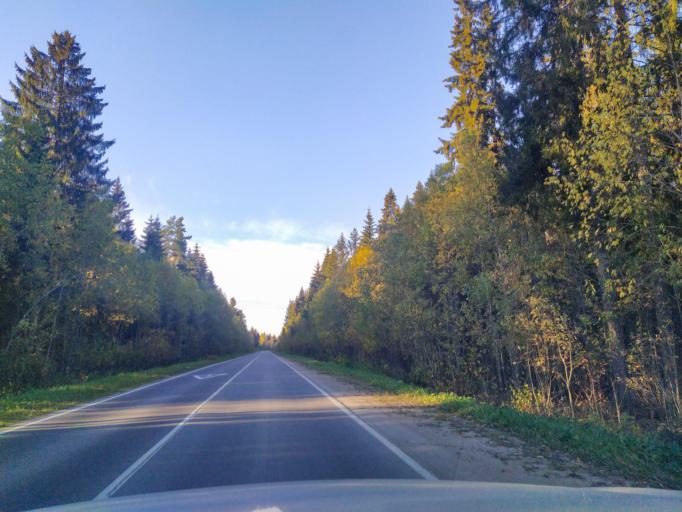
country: RU
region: Leningrad
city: Siverskiy
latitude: 59.3039
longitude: 30.0344
